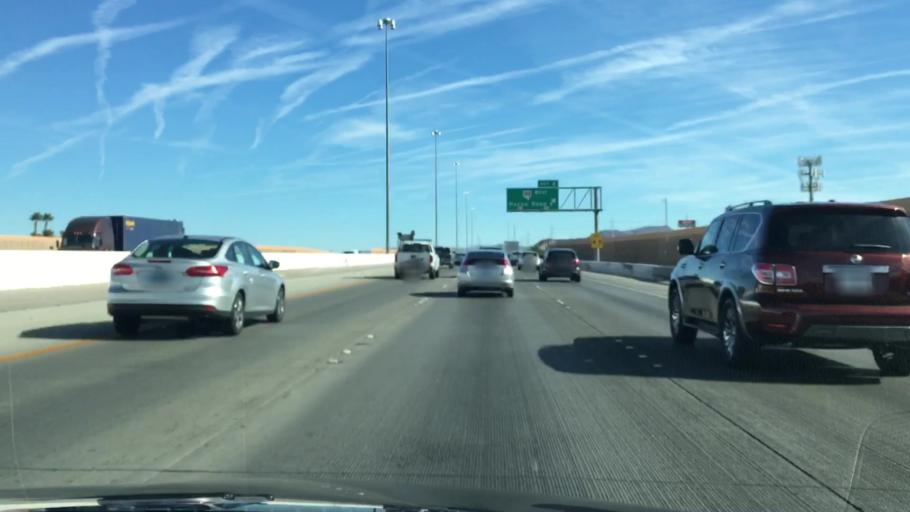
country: US
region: Nevada
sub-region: Clark County
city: Whitney
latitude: 36.0234
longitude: -115.1073
